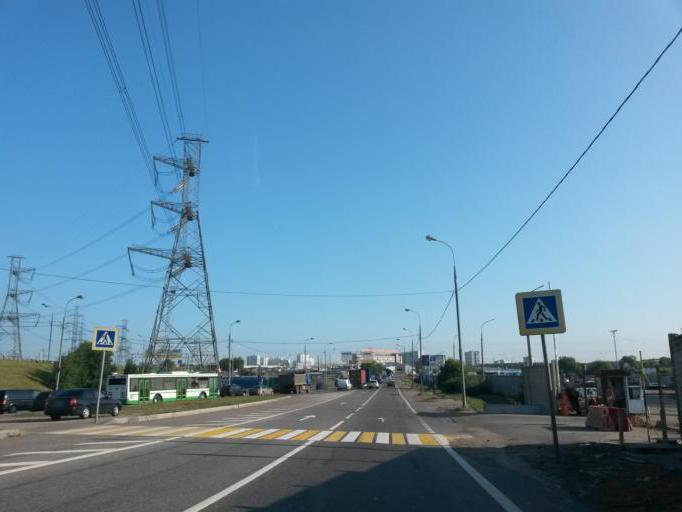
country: RU
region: Moscow
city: Annino
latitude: 55.5687
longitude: 37.6010
